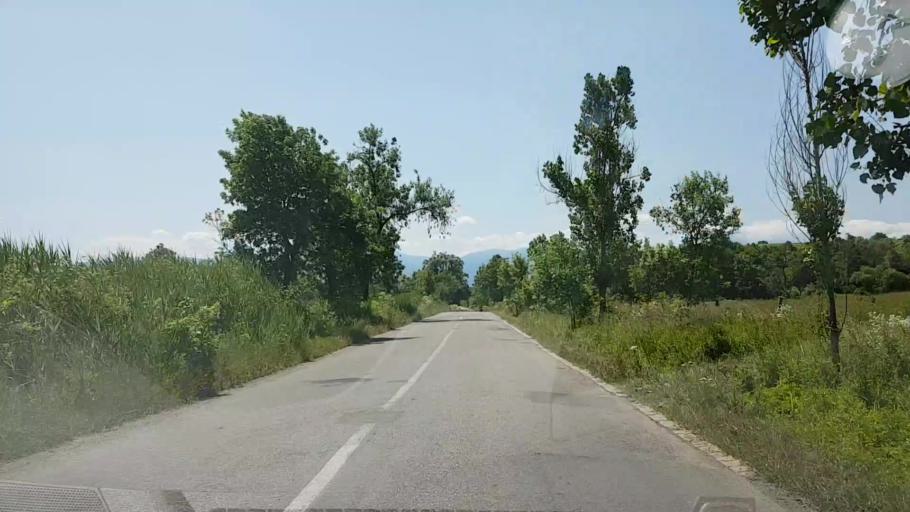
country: RO
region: Brasov
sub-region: Comuna Voila
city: Voila
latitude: 45.8513
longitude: 24.8321
